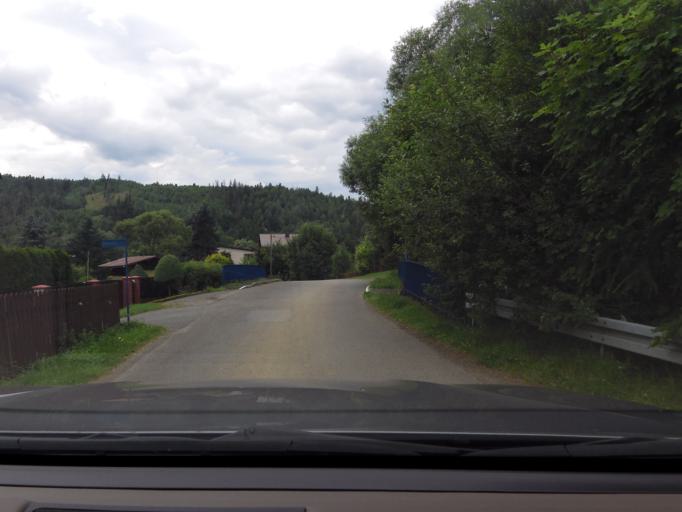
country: PL
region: Silesian Voivodeship
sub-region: Powiat zywiecki
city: Rajcza
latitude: 49.5066
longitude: 19.1134
